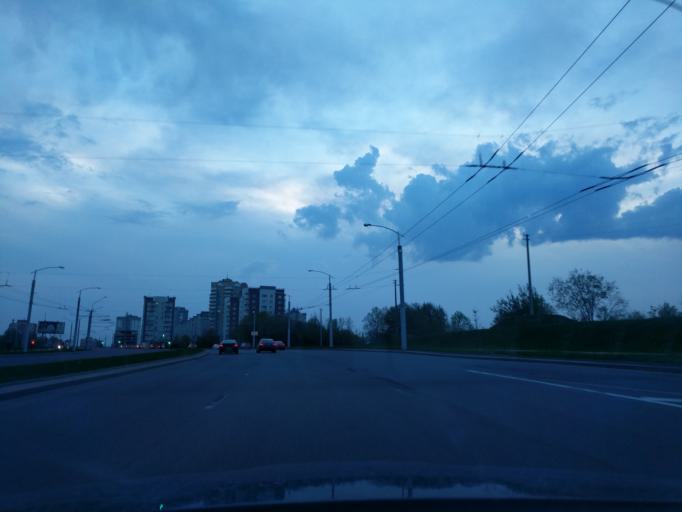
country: BY
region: Minsk
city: Novoye Medvezhino
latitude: 53.8722
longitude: 27.4903
